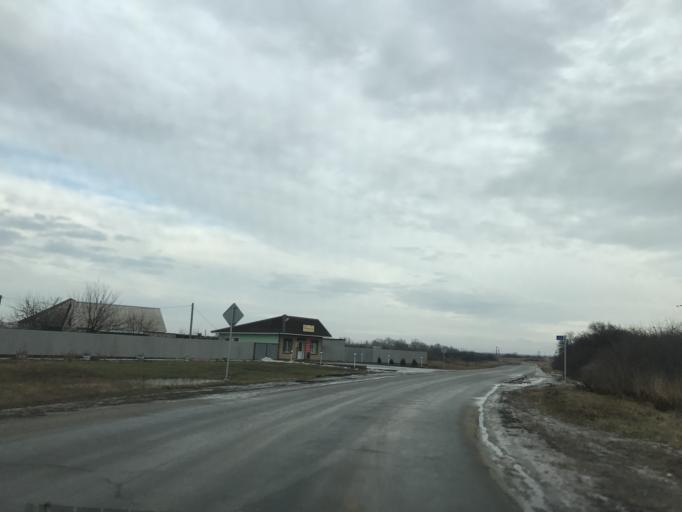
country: RU
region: Rostov
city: Glubokiy
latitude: 48.4835
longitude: 40.3087
